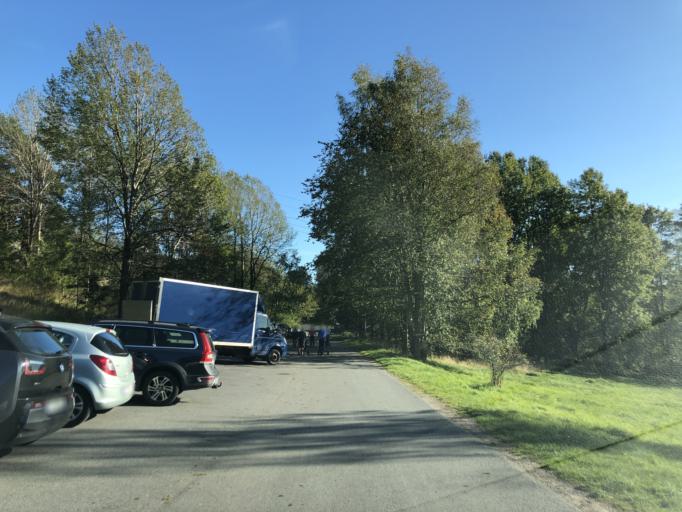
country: SE
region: Vaestra Goetaland
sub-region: Molndal
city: Moelndal
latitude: 57.6832
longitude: 12.0217
